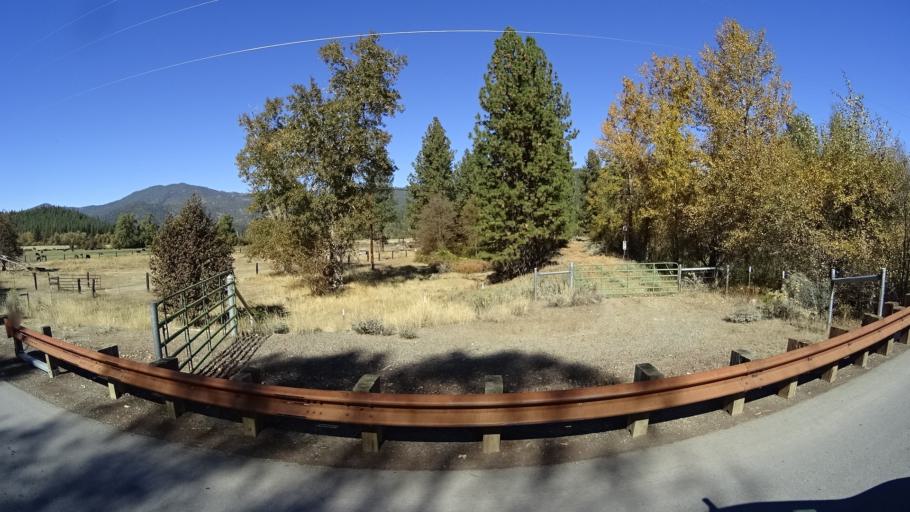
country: US
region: California
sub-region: Siskiyou County
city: Yreka
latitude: 41.6241
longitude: -122.9659
